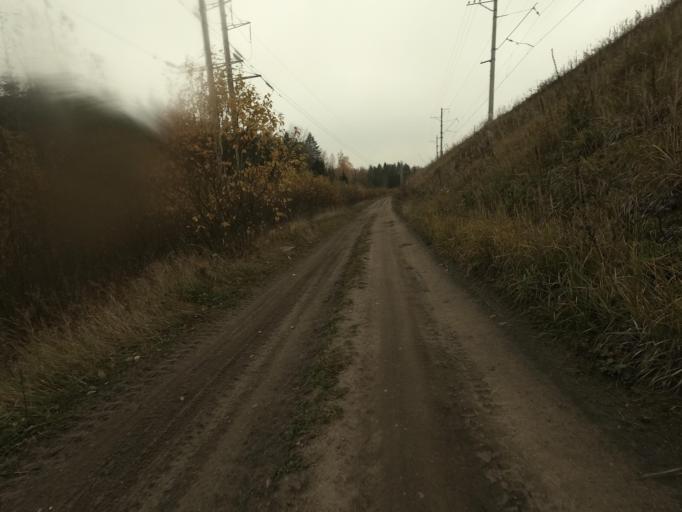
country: RU
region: Leningrad
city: Pavlovo
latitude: 59.7688
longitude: 30.9167
